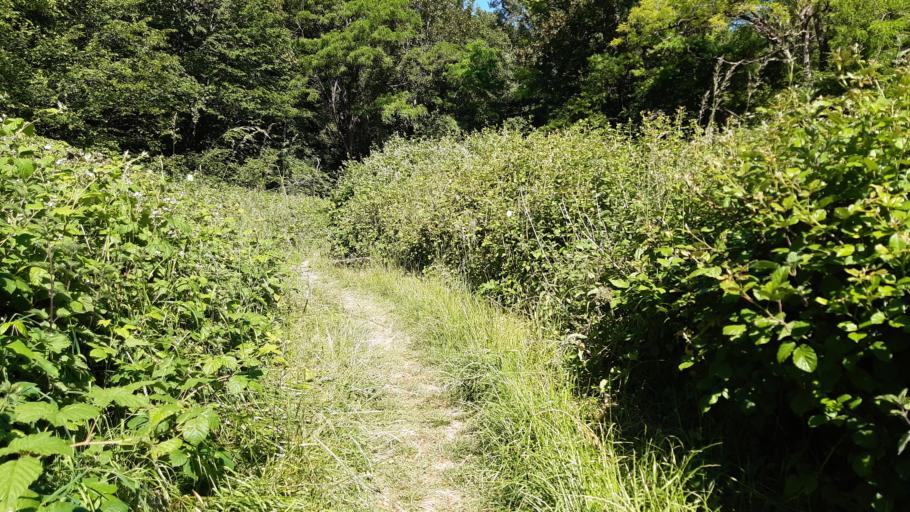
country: FR
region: Centre
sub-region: Departement d'Indre-et-Loire
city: Mettray
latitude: 47.4373
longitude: 0.6585
